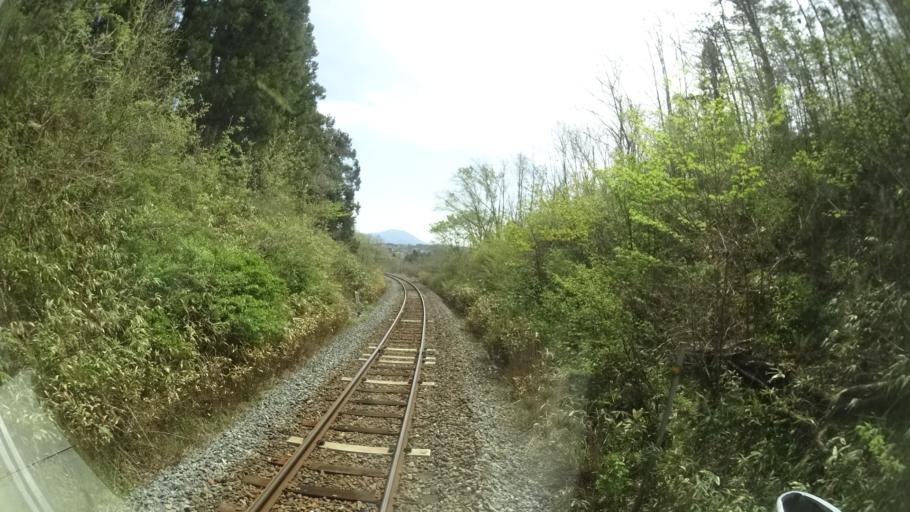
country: JP
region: Iwate
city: Ichinoseki
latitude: 38.9934
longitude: 141.2813
